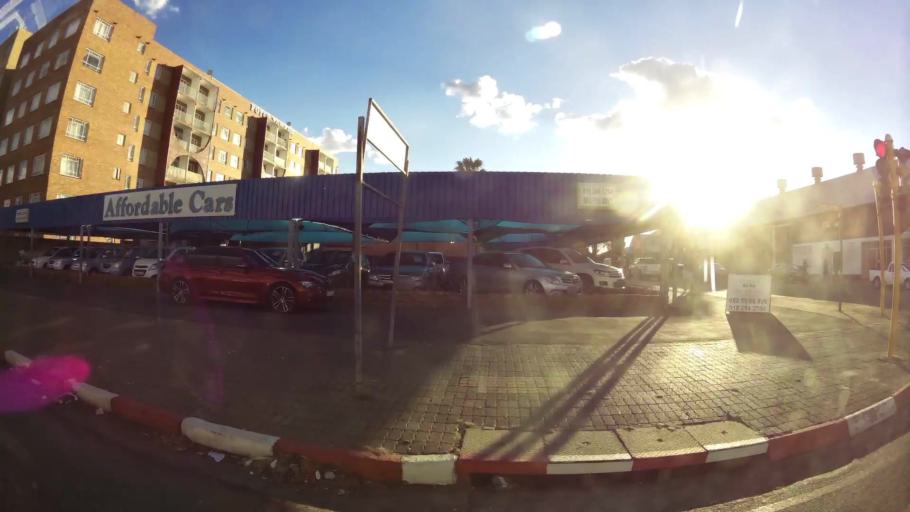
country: ZA
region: North-West
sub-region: Dr Kenneth Kaunda District Municipality
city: Potchefstroom
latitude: -26.7174
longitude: 27.0968
